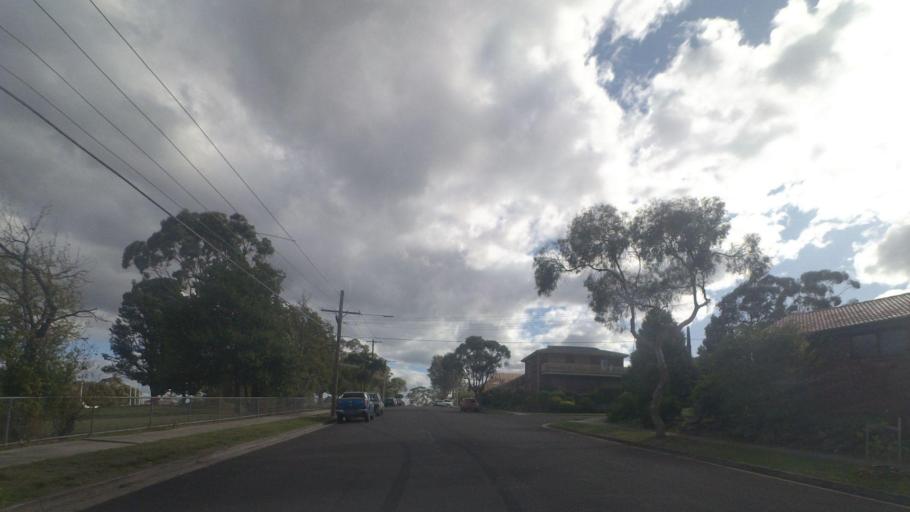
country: AU
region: Victoria
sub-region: Whitehorse
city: Vermont South
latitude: -37.8513
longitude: 145.1837
